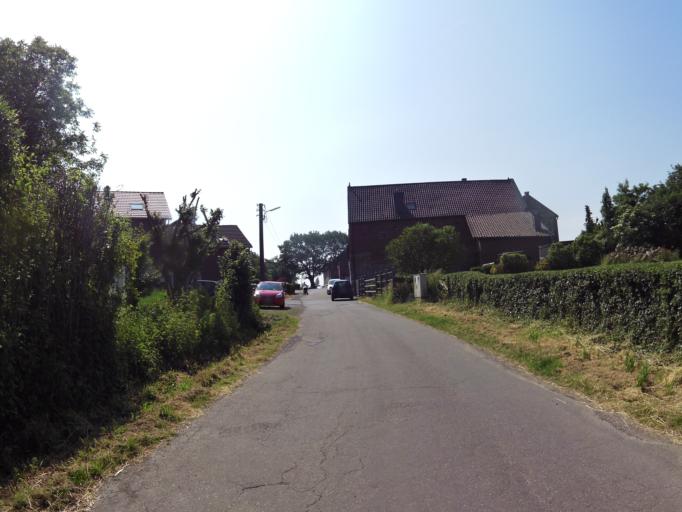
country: DE
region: North Rhine-Westphalia
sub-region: Regierungsbezirk Koln
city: Aachen
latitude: 50.8118
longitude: 6.0787
